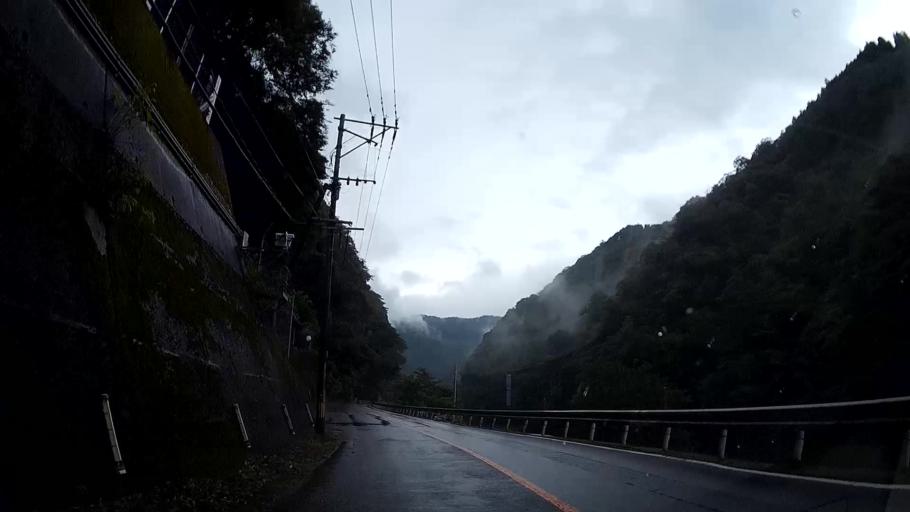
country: JP
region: Oita
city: Hita
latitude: 33.1798
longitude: 131.0180
